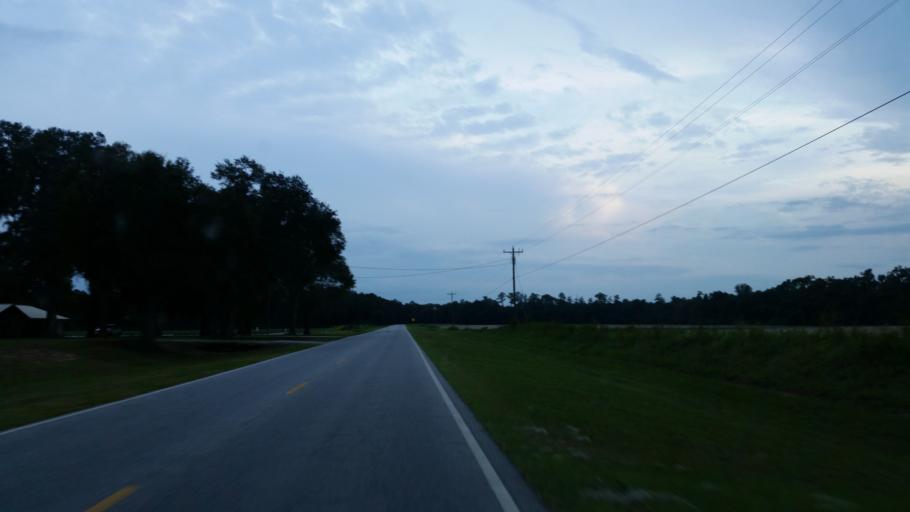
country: US
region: Georgia
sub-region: Echols County
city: Statenville
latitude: 30.6553
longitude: -83.1842
